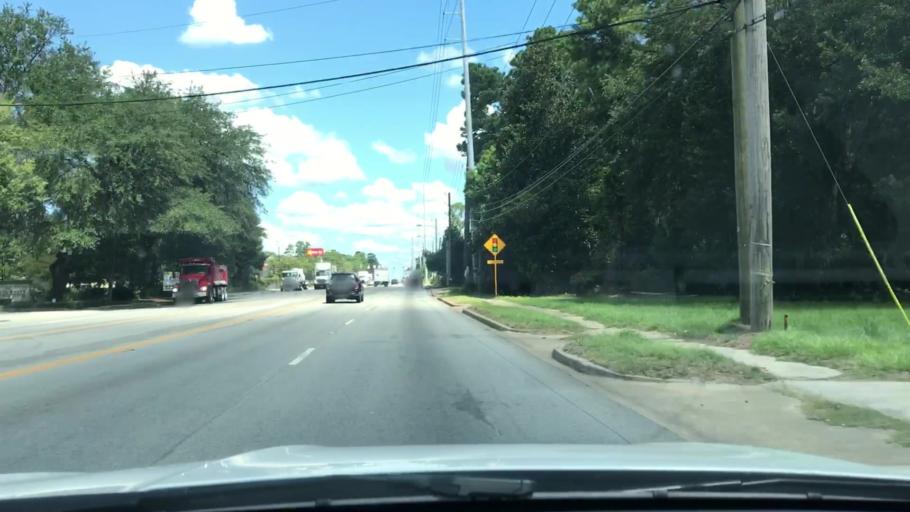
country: US
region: South Carolina
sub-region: Berkeley County
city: Hanahan
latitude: 32.8996
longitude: -79.9855
